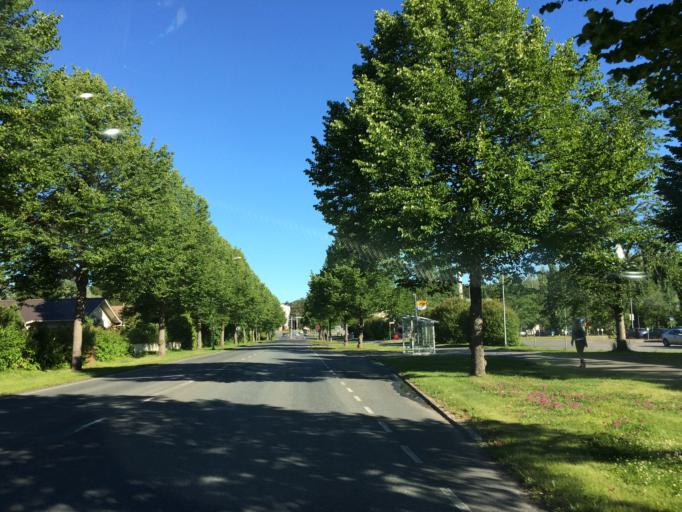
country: FI
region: Haeme
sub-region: Haemeenlinna
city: Haemeenlinna
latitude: 60.9820
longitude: 24.4184
